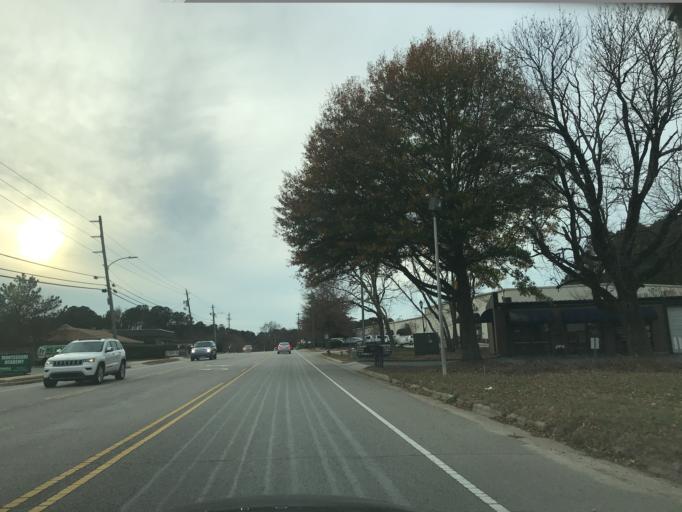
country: US
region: North Carolina
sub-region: Wake County
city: Cary
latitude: 35.7912
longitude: -78.7688
